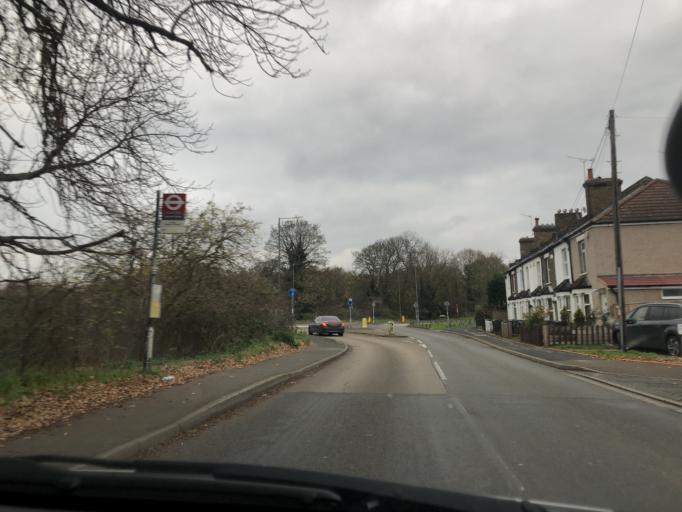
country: GB
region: England
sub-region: Kent
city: Swanley
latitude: 51.4296
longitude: 0.1816
